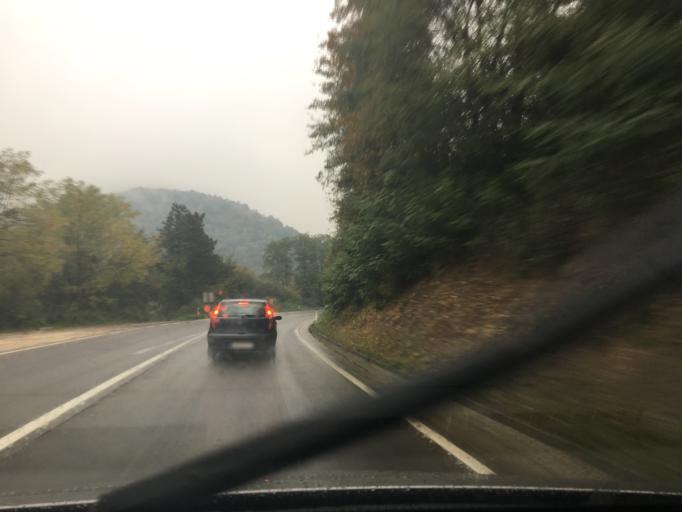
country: RS
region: Central Serbia
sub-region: Pcinjski Okrug
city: Vladicin Han
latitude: 42.7376
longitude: 22.0587
